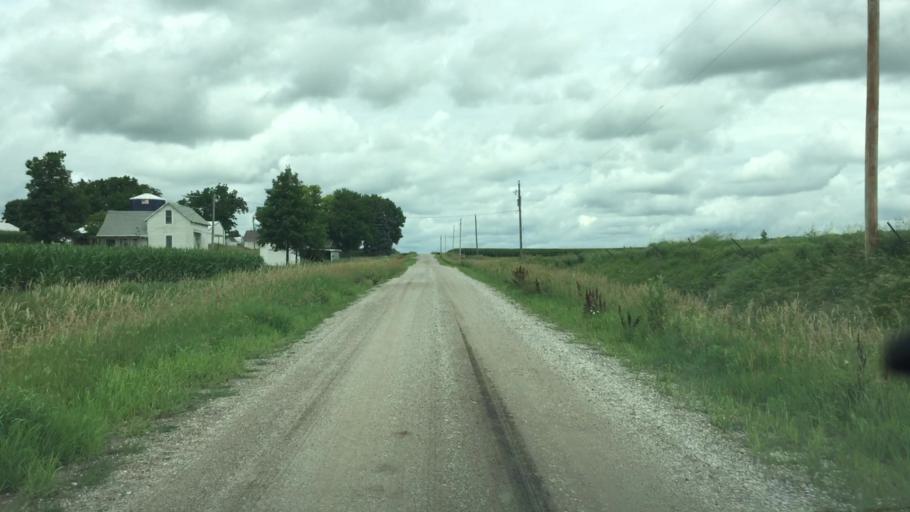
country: US
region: Iowa
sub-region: Jasper County
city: Monroe
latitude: 41.5674
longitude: -93.1208
